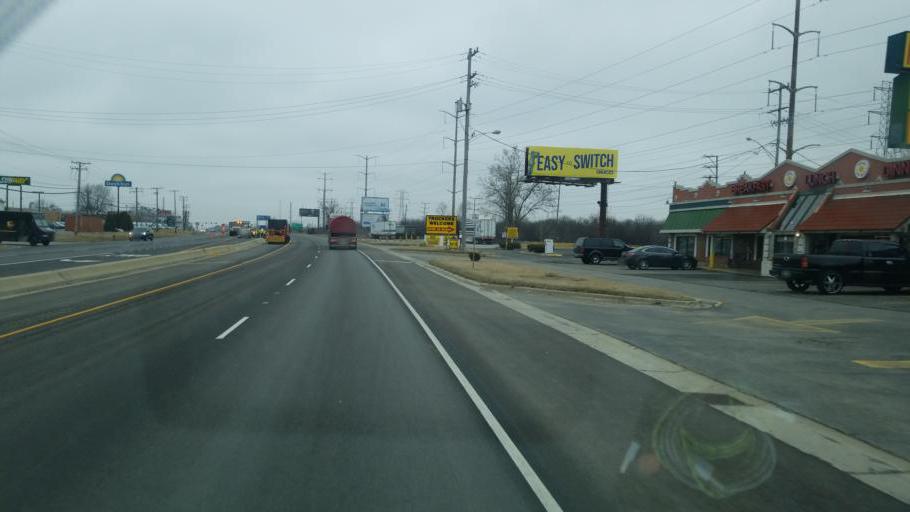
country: US
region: Illinois
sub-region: Lake County
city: Knollwood
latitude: 42.3035
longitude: -87.8755
